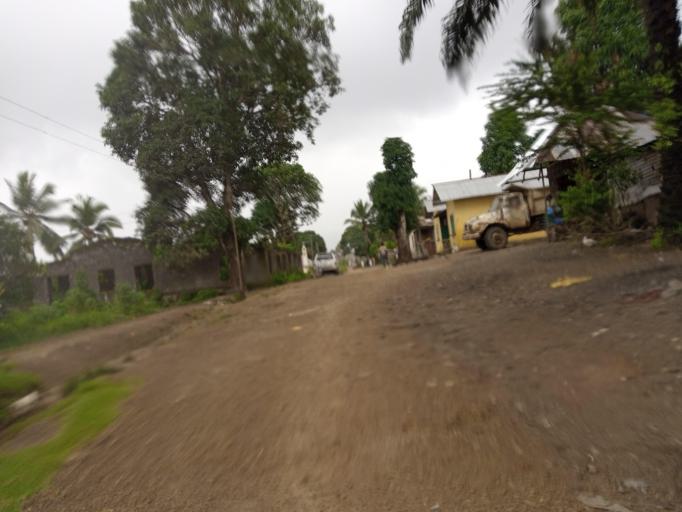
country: SL
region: Eastern Province
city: Kenema
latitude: 7.8798
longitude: -11.1785
